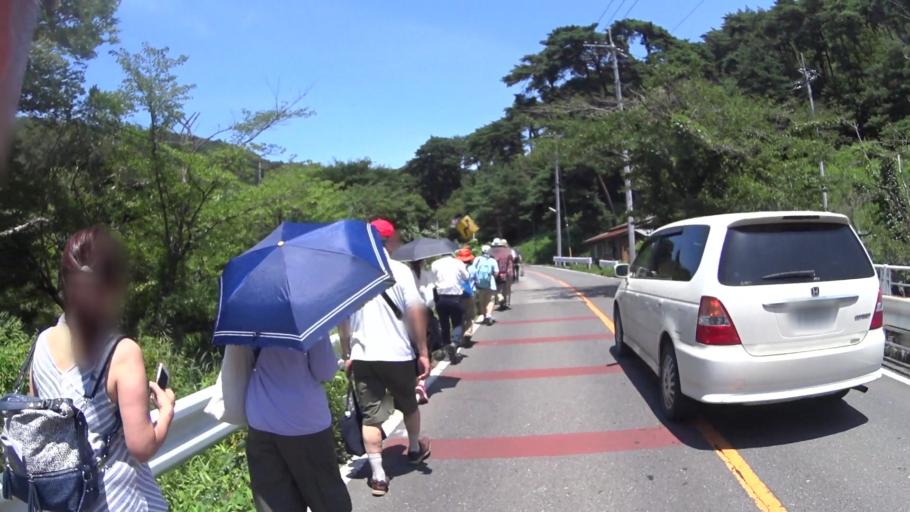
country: JP
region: Gunma
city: Ota
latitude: 36.3093
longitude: 139.3732
